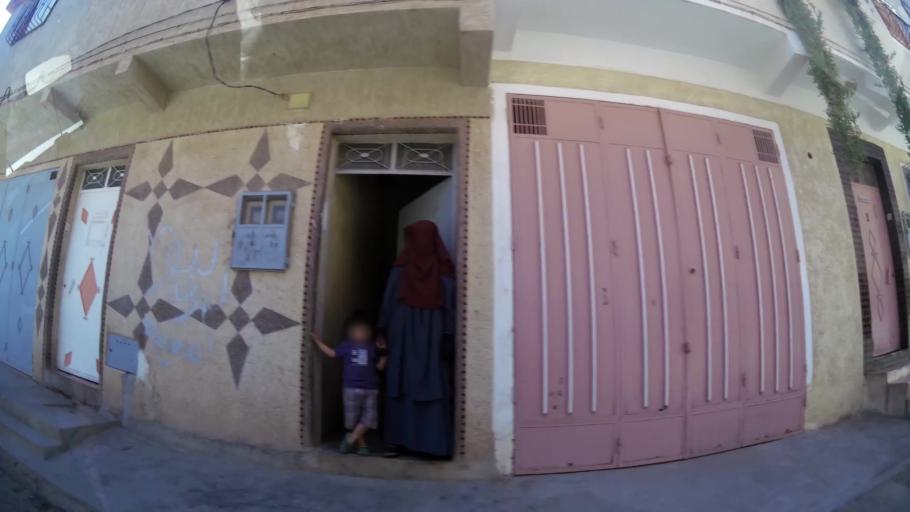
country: MA
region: Oriental
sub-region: Oujda-Angad
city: Oujda
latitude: 34.6586
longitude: -1.8817
